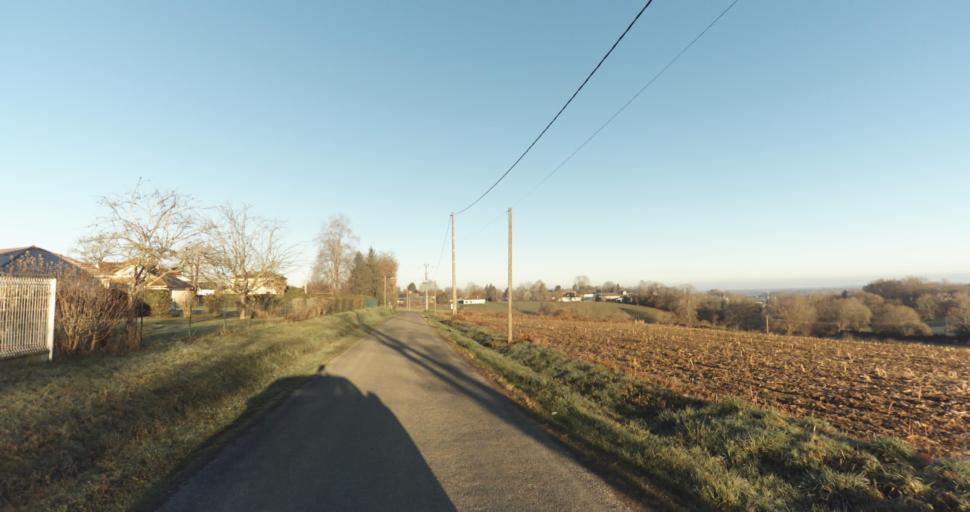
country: FR
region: Aquitaine
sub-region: Departement des Pyrenees-Atlantiques
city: Morlaas
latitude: 43.3311
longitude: -0.2676
